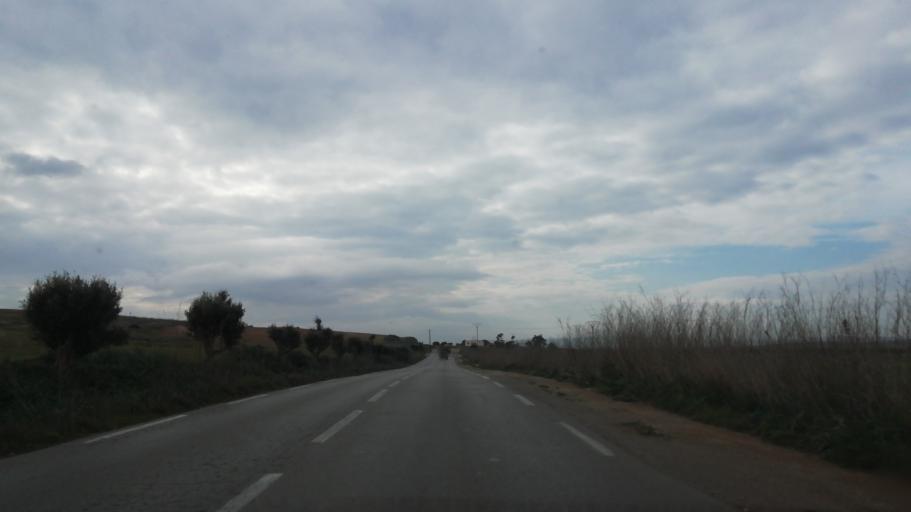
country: DZ
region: Oran
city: Ain el Bya
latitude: 35.7498
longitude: -0.3529
